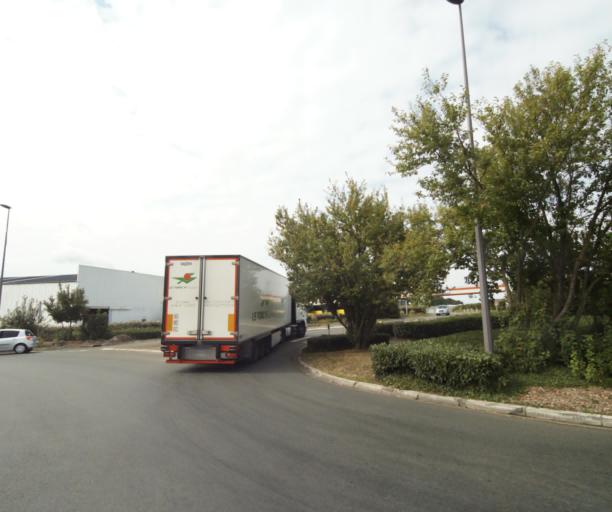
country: FR
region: Pays de la Loire
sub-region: Departement de la Sarthe
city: Solesmes
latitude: 47.8278
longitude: -0.3088
